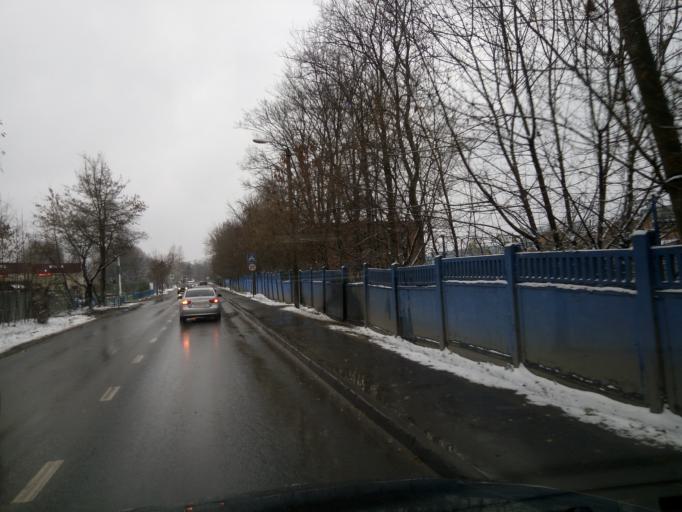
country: RU
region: Moskovskaya
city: Skhodnya
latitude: 55.9430
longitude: 37.2802
